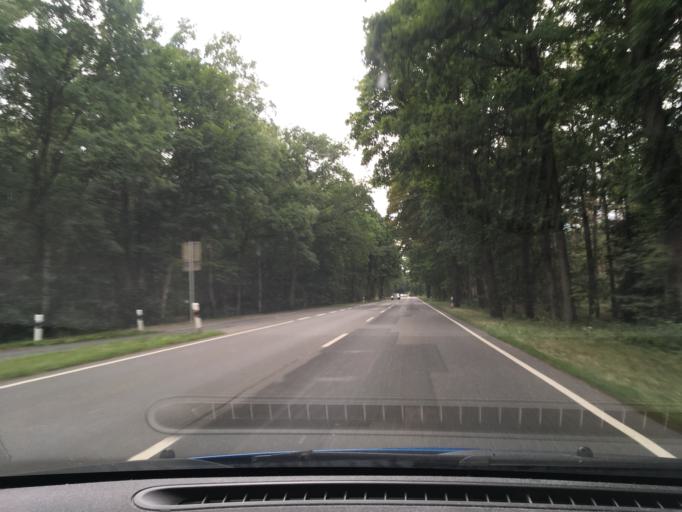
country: DE
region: Lower Saxony
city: Kakenstorf
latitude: 53.3019
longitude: 9.7485
